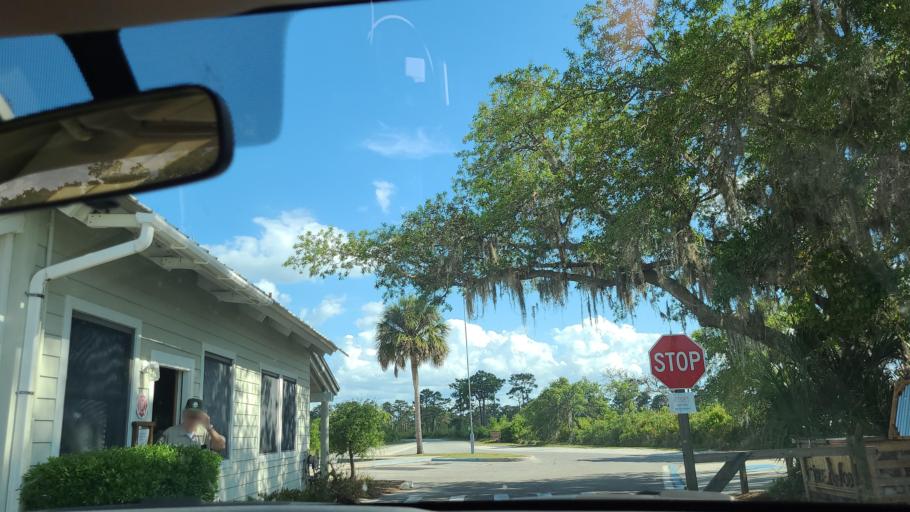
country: US
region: Florida
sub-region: Osceola County
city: Poinciana
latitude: 27.9693
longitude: -81.3803
